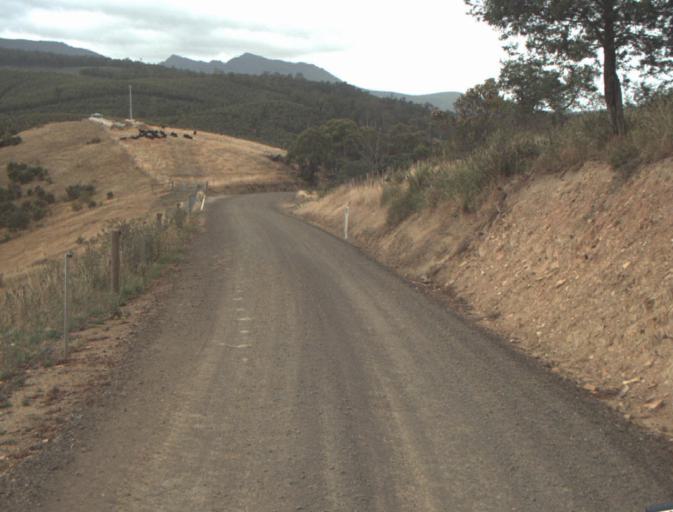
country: AU
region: Tasmania
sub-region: Northern Midlands
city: Evandale
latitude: -41.4710
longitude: 147.5340
